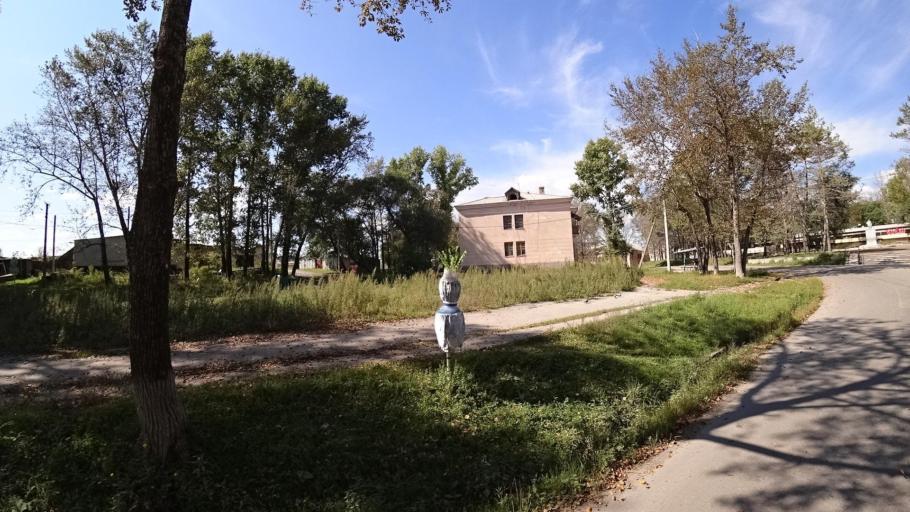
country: RU
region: Jewish Autonomous Oblast
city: Londoko
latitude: 49.0103
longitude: 131.8837
